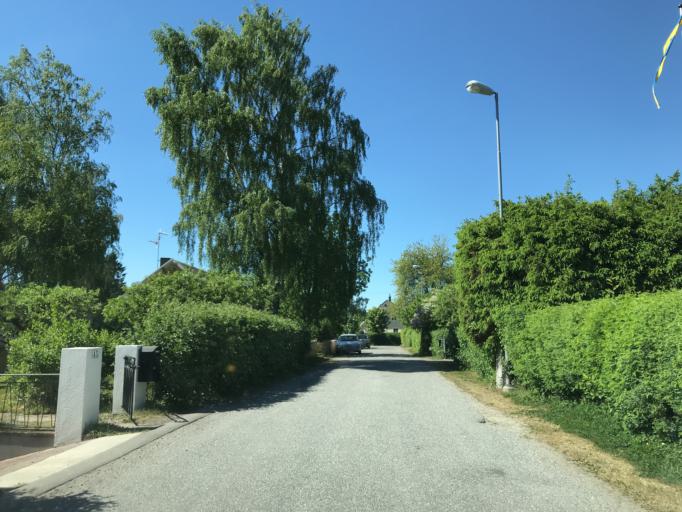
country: SE
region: Stockholm
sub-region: Sollentuna Kommun
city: Sollentuna
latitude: 59.4221
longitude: 17.9611
